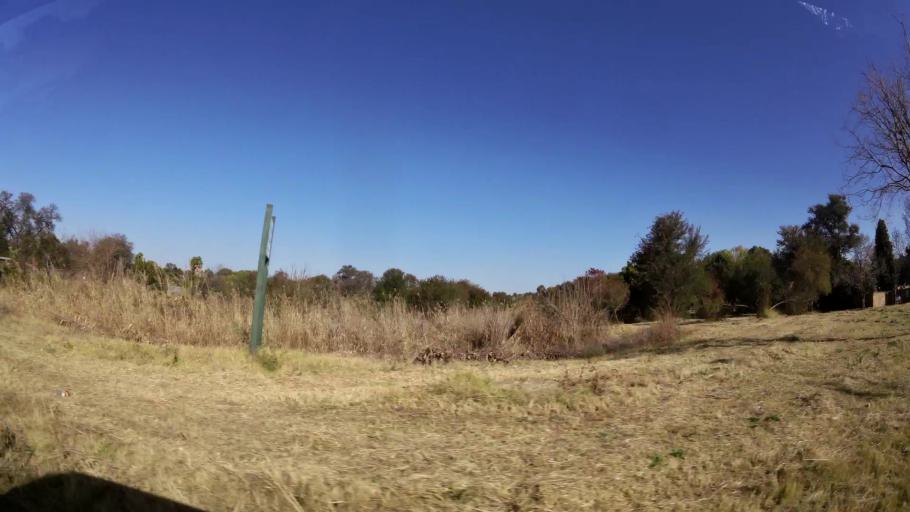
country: ZA
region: Gauteng
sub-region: City of Tshwane Metropolitan Municipality
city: Pretoria
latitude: -25.7277
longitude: 28.2617
